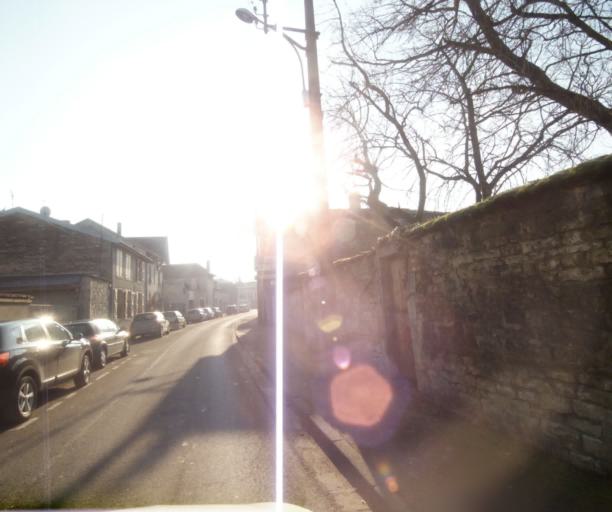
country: FR
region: Champagne-Ardenne
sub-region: Departement de la Haute-Marne
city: Wassy
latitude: 48.4999
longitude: 4.9454
